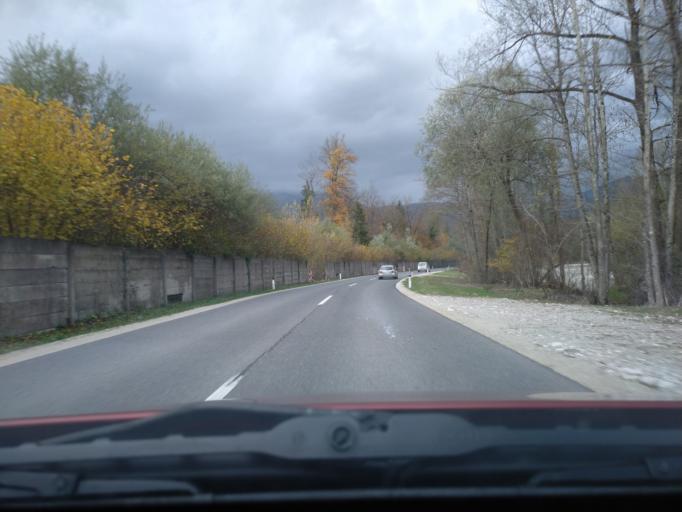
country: SI
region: Kamnik
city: Mekinje
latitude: 46.2404
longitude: 14.6048
